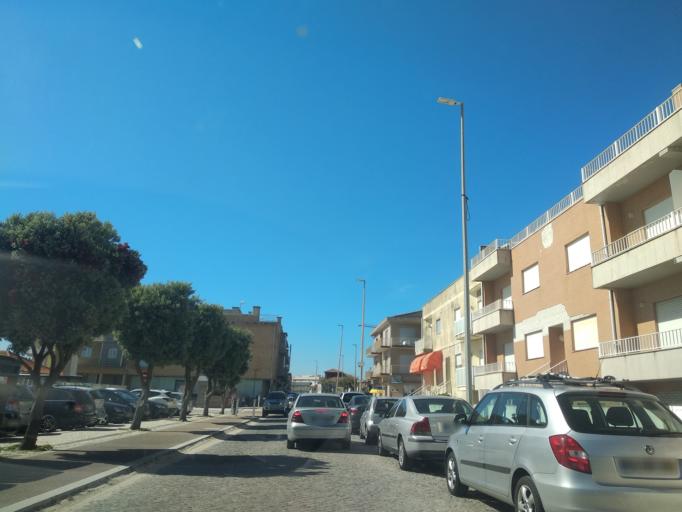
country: PT
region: Braga
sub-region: Esposende
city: Apulia
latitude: 41.4832
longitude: -8.7766
